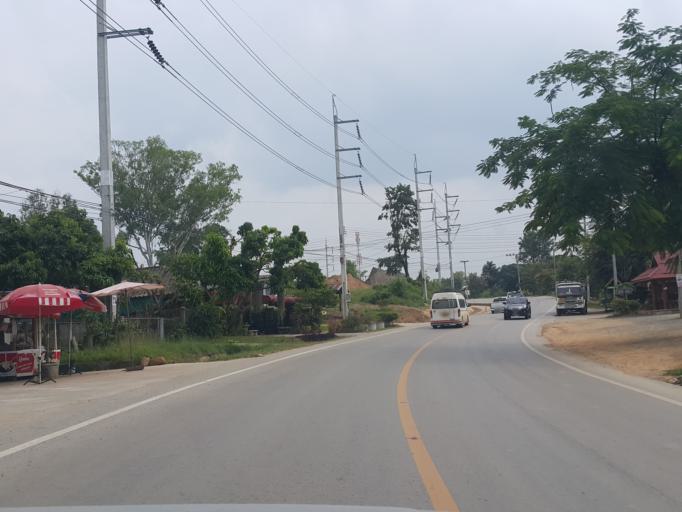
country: TH
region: Chiang Mai
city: Mae Taeng
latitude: 19.0937
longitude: 98.8566
